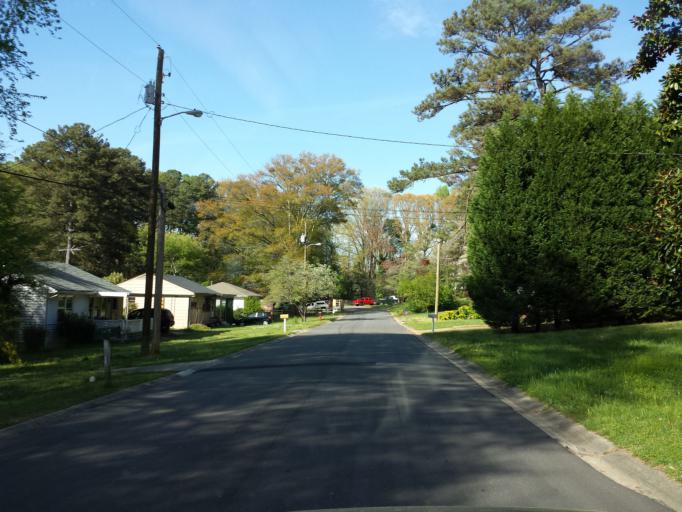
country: US
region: Georgia
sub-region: Cobb County
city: Marietta
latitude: 33.9658
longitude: -84.5288
